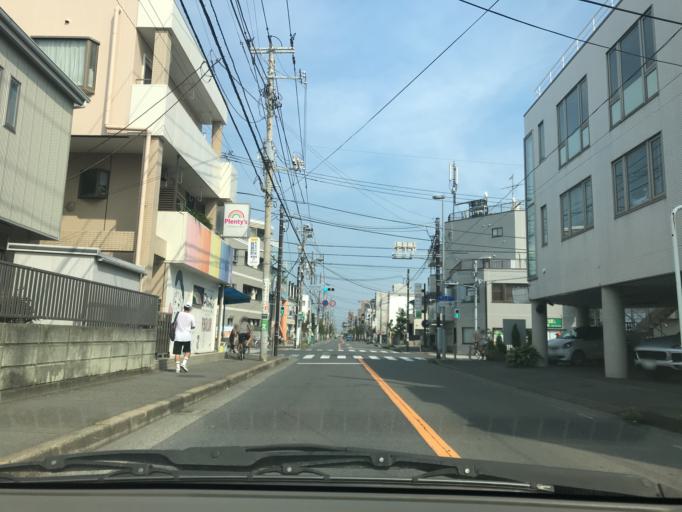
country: JP
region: Kanagawa
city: Chigasaki
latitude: 35.3248
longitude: 139.4076
